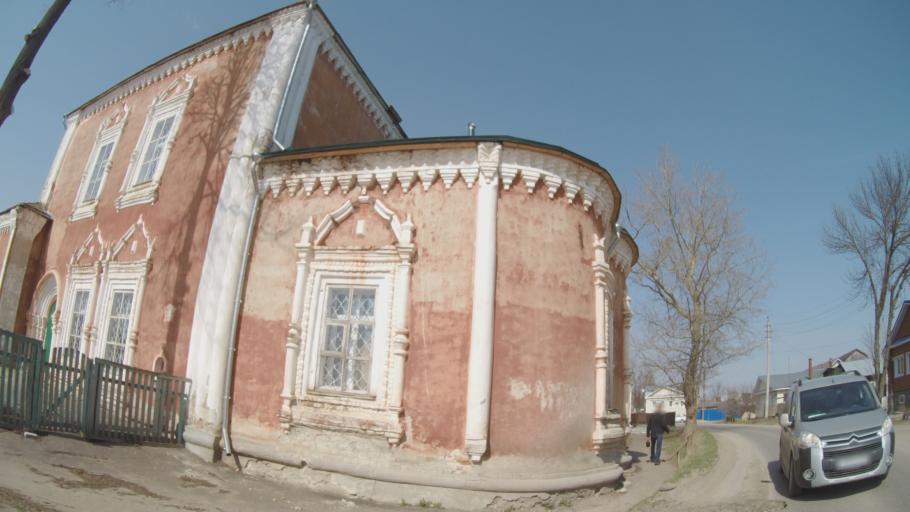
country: RU
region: Nizjnij Novgorod
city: Arzamas
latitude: 55.3864
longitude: 43.8237
